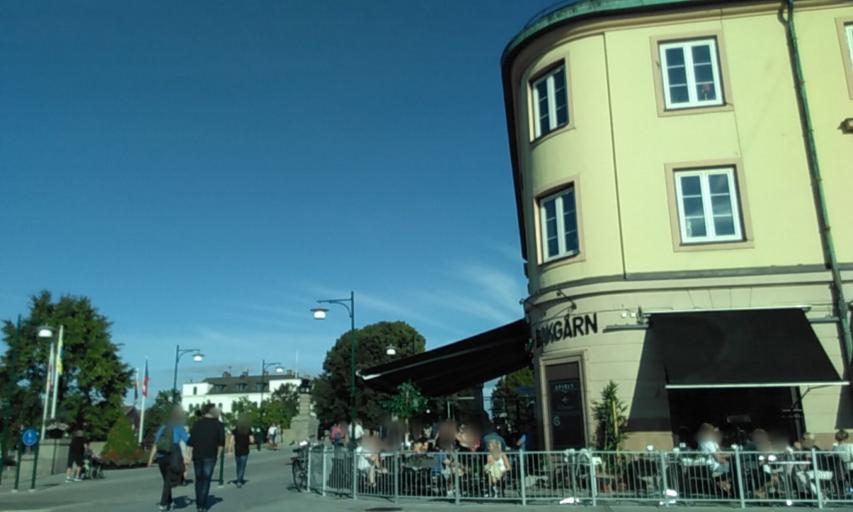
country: SE
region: Vaestra Goetaland
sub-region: Lidkopings Kommun
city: Lidkoping
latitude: 58.5035
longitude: 13.1585
